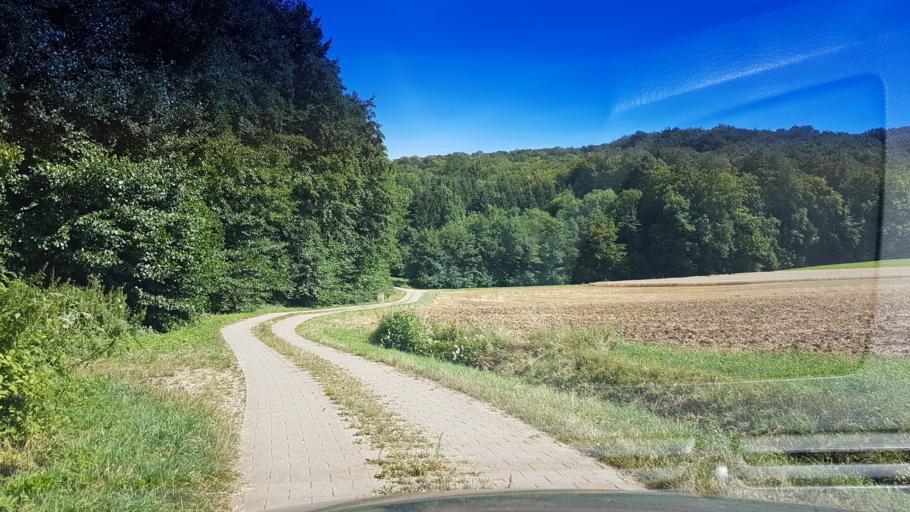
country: DE
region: Bavaria
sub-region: Upper Franconia
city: Schesslitz
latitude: 49.9435
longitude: 11.0513
